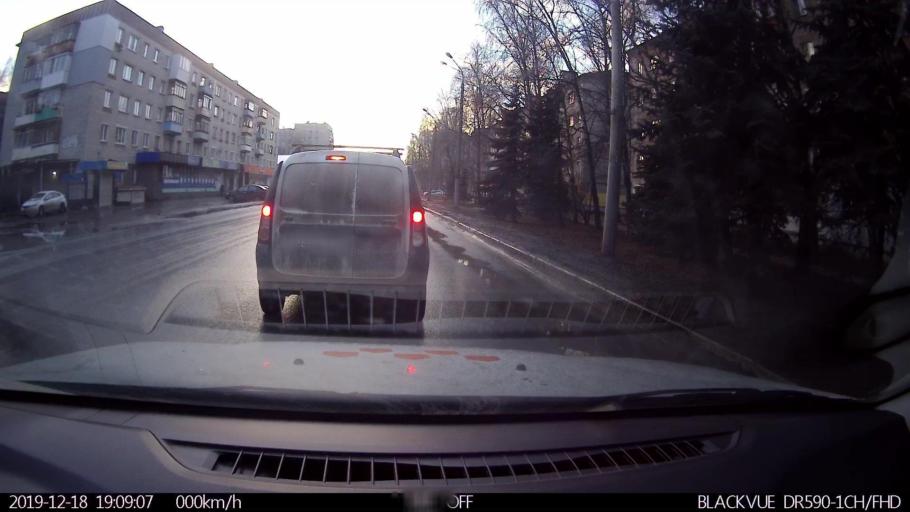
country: RU
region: Nizjnij Novgorod
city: Nizhniy Novgorod
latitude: 56.3191
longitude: 43.8673
